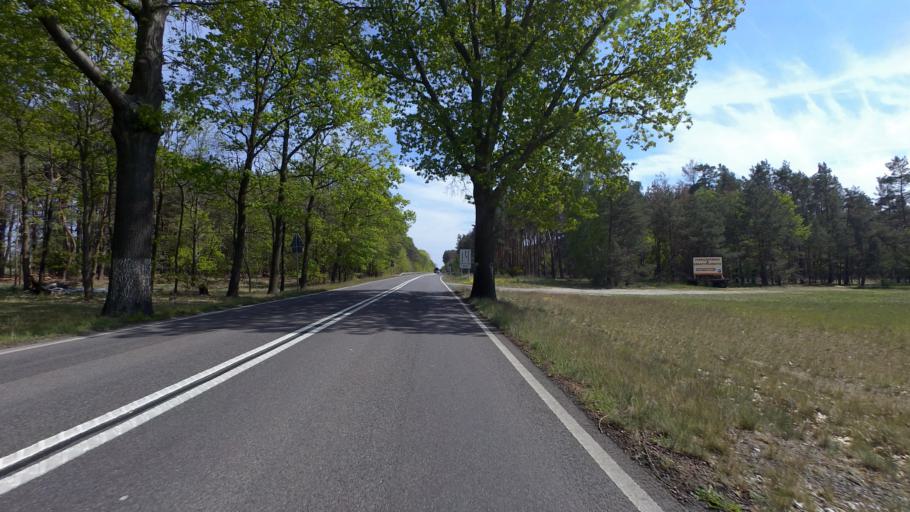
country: DE
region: Brandenburg
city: Heinersbruck
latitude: 51.6956
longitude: 14.4922
